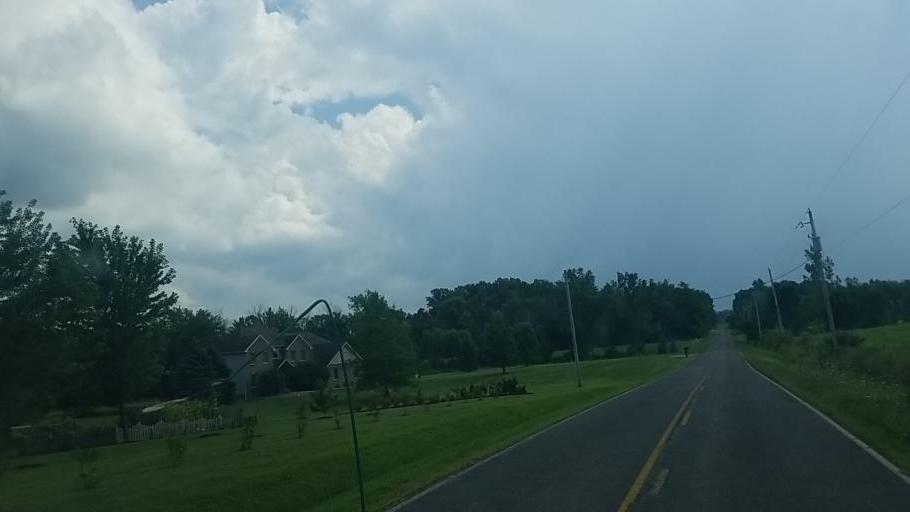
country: US
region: Ohio
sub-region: Medina County
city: Medina
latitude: 41.1419
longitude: -81.9545
